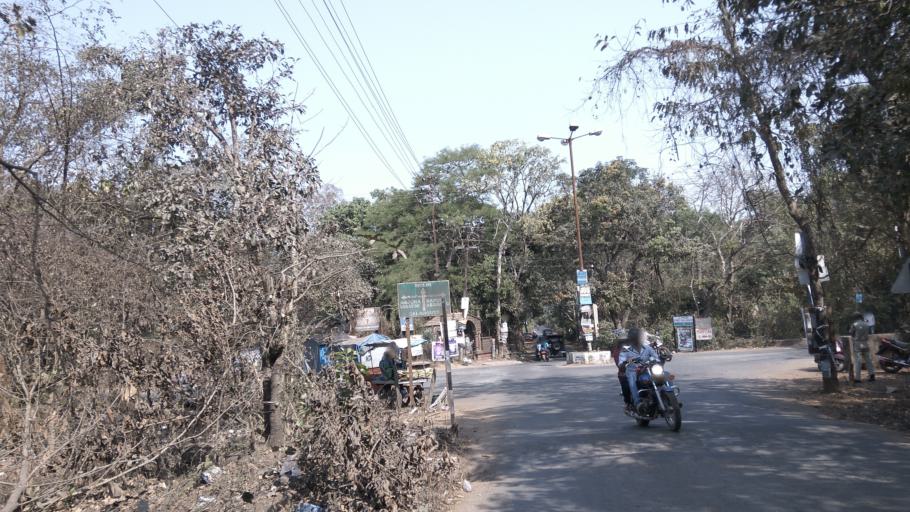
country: IN
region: Goa
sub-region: North Goa
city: Vagator
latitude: 15.5873
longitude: 73.7603
